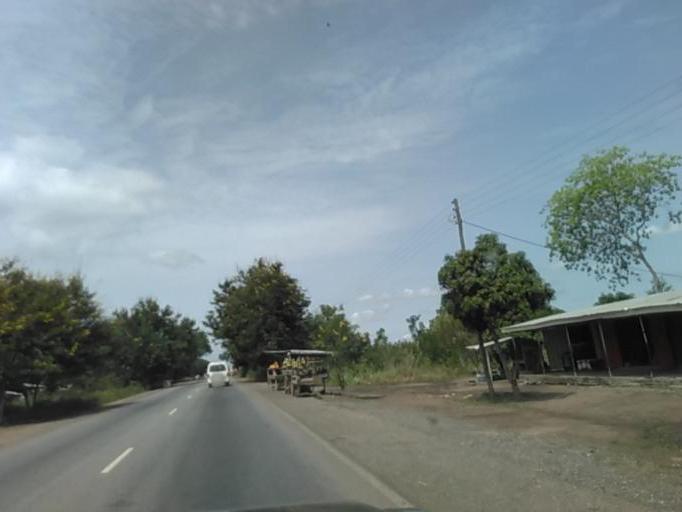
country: GH
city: Akropong
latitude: 6.0991
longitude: 0.0455
